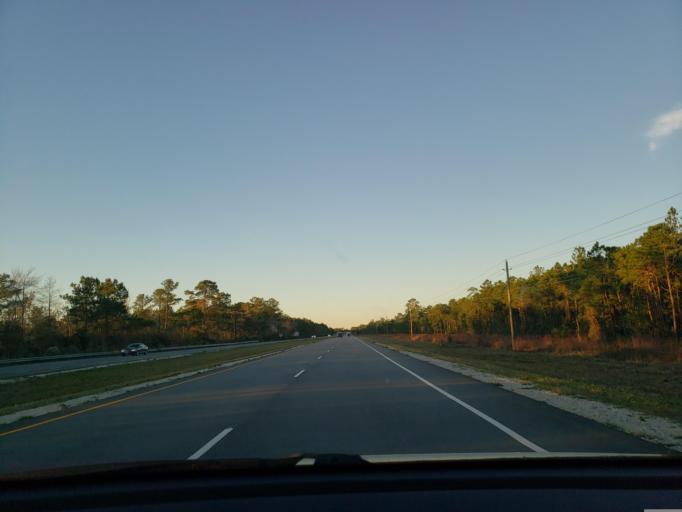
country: US
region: North Carolina
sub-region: Onslow County
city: Sneads Ferry
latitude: 34.6000
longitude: -77.4815
